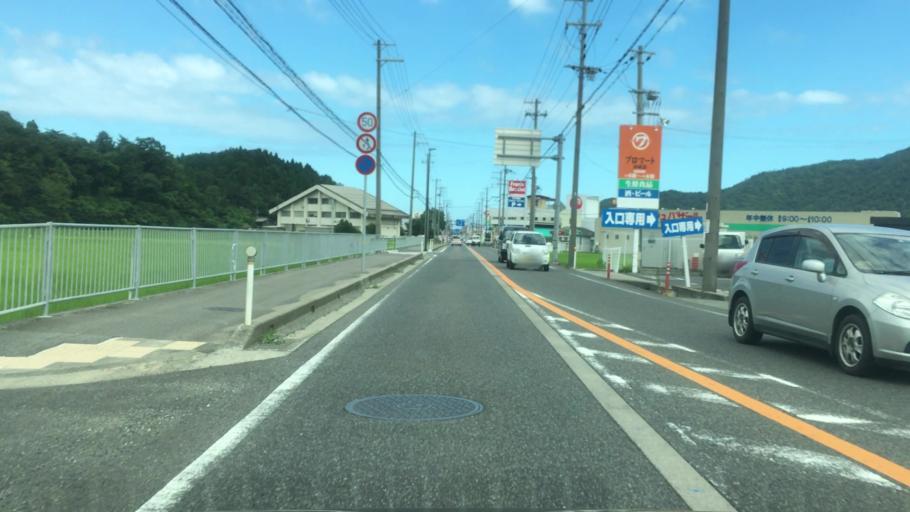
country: JP
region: Tottori
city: Tottori
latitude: 35.6148
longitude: 134.4660
